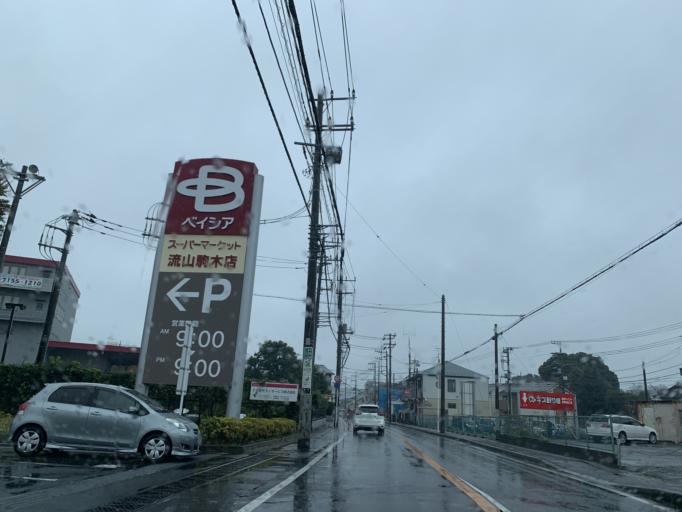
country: JP
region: Chiba
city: Kashiwa
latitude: 35.8806
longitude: 139.9368
